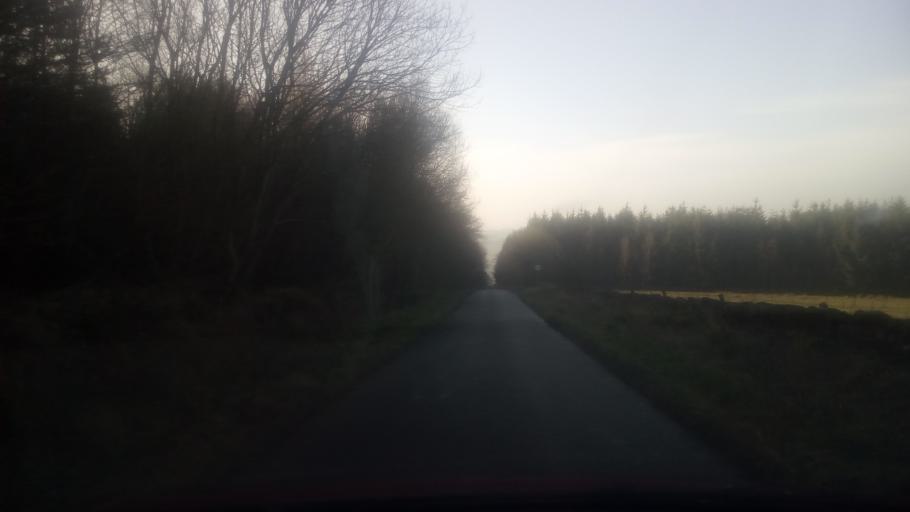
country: GB
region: Scotland
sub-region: The Scottish Borders
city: Jedburgh
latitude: 55.4841
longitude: -2.5861
